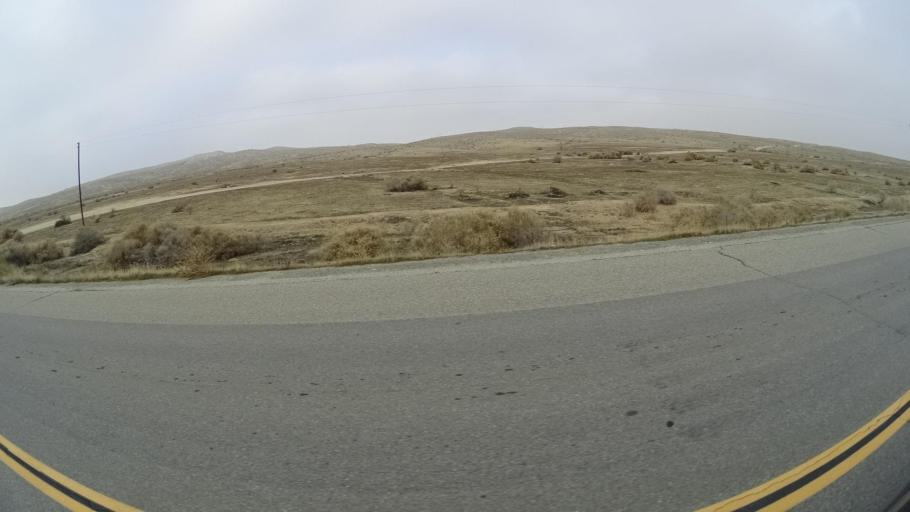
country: US
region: California
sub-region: Kern County
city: Maricopa
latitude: 35.1302
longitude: -119.3717
